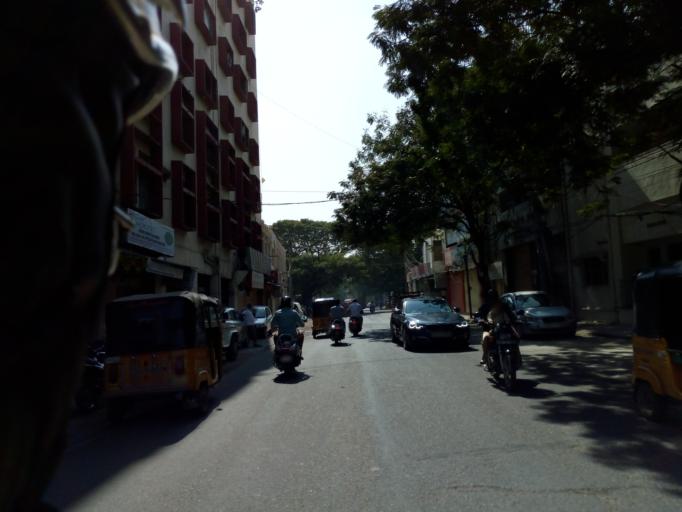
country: IN
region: Telangana
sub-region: Hyderabad
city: Malkajgiri
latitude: 17.4297
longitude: 78.4925
